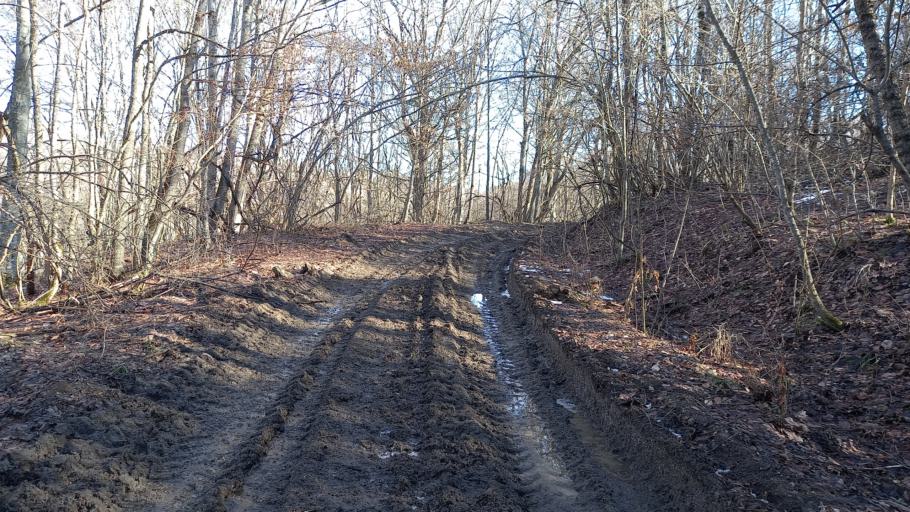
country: RU
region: Adygeya
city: Kamennomostskiy
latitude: 44.2830
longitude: 40.3338
